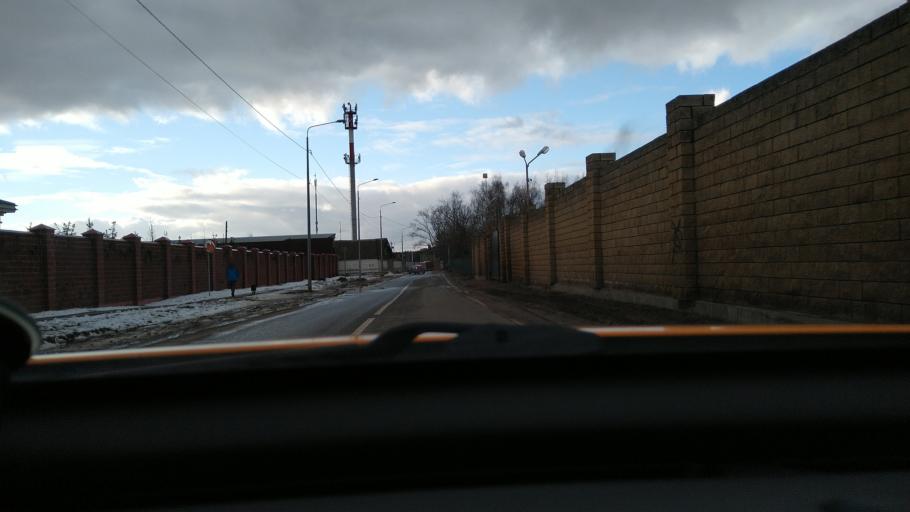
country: RU
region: Moskovskaya
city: Petrovo-Dal'neye
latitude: 55.7725
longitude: 37.2036
